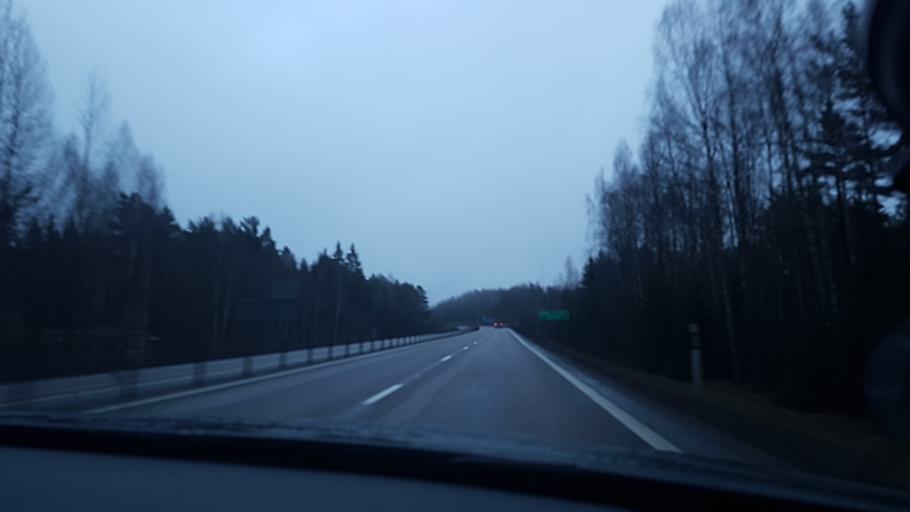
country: SE
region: Vaermland
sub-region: Kristinehamns Kommun
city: Kristinehamn
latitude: 59.3215
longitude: 14.1348
